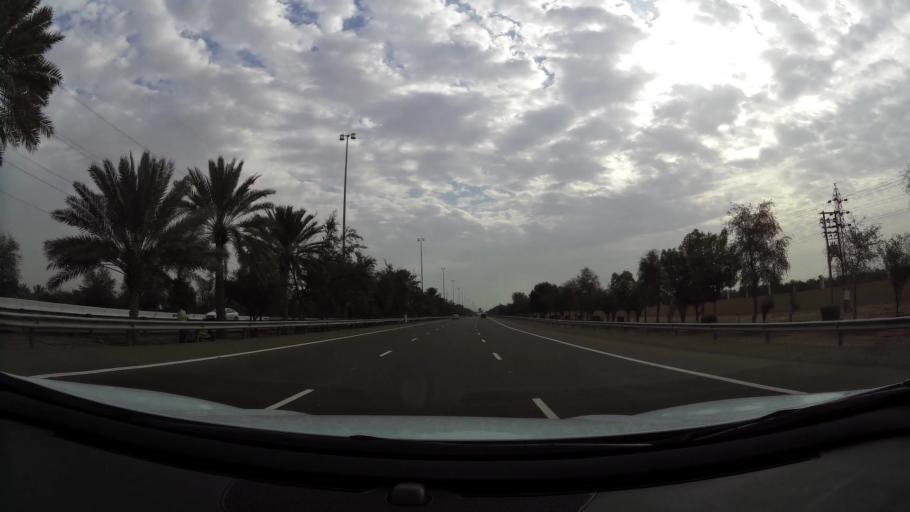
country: AE
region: Abu Dhabi
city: Al Ain
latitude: 24.2092
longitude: 55.4465
